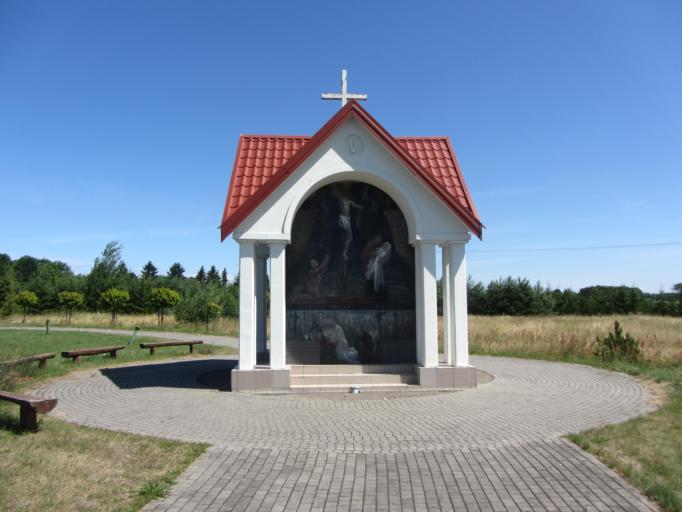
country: LT
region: Vilnius County
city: Elektrenai
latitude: 54.8405
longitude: 24.5673
